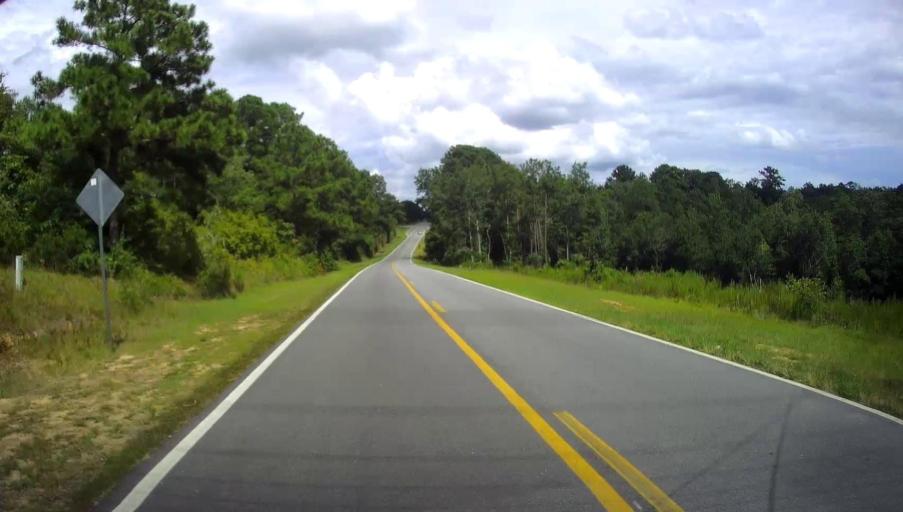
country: US
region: Georgia
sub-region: Chattahoochee County
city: Cusseta
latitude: 32.3075
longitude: -84.7586
